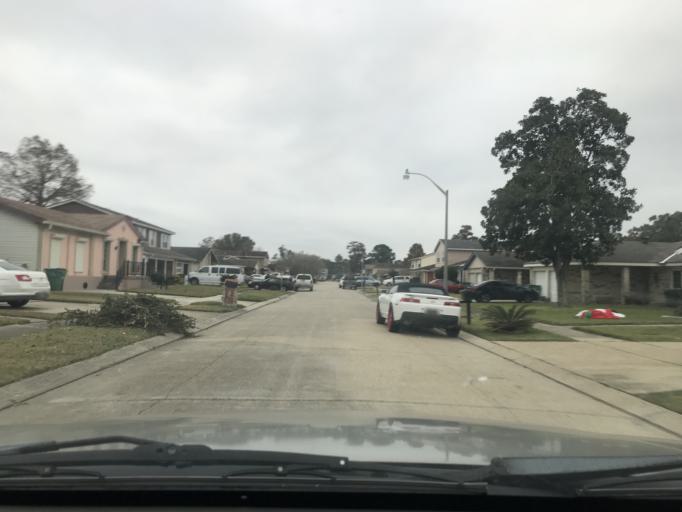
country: US
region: Louisiana
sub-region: Jefferson Parish
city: Woodmere
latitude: 29.8664
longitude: -90.0784
